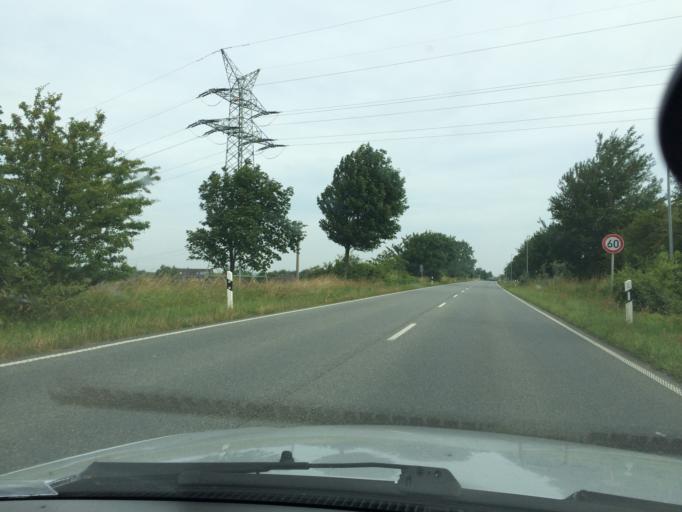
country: DE
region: Schleswig-Holstein
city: Jarplund-Weding
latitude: 54.7494
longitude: 9.4367
